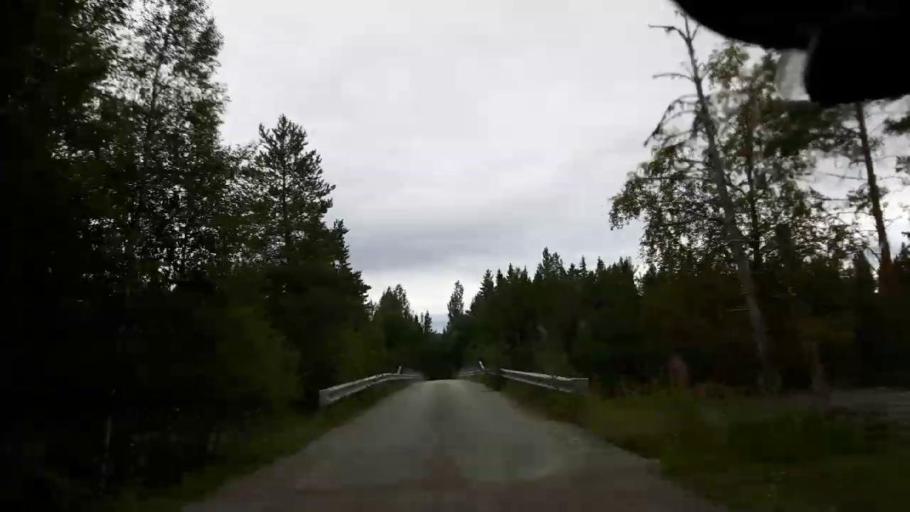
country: SE
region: Vaesternorrland
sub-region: Ange Kommun
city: Ange
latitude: 62.8186
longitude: 15.7131
